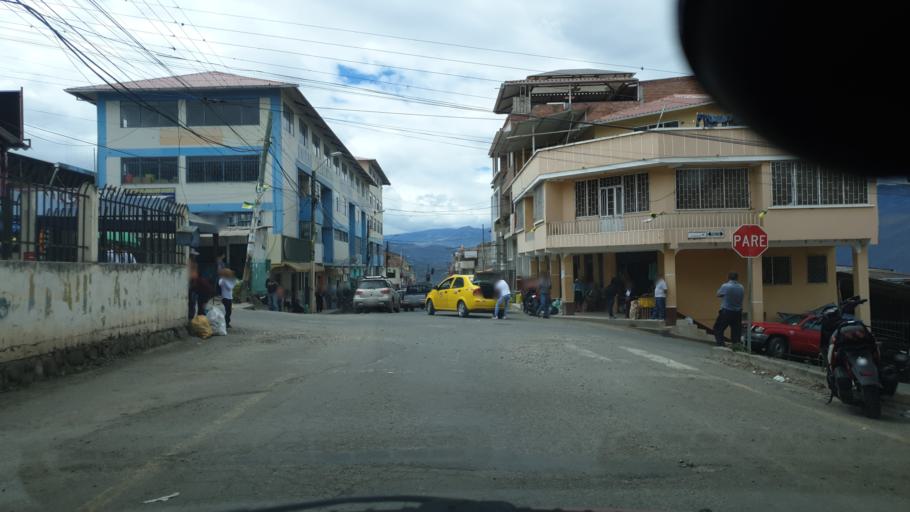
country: EC
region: Azuay
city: Cuenca
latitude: -3.2764
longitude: -79.3149
